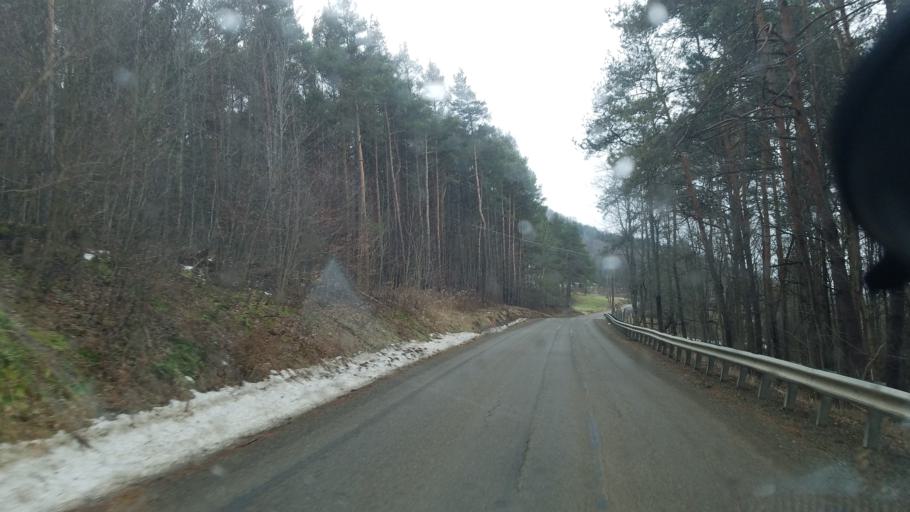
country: US
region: New York
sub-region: Allegany County
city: Wellsville
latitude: 41.9555
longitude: -77.8343
